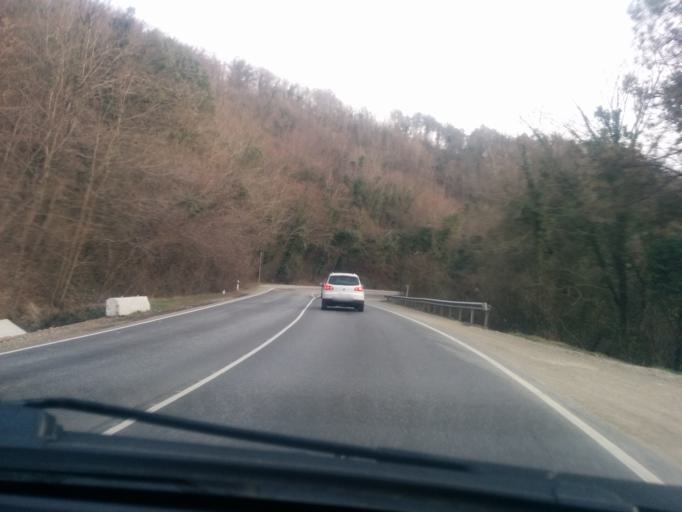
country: RU
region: Krasnodarskiy
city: Agoy
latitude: 44.1399
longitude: 39.0540
